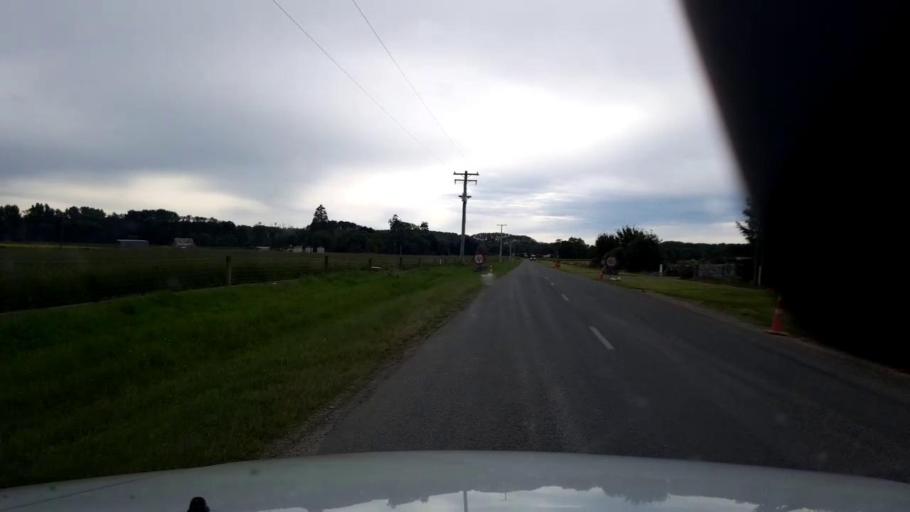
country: NZ
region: Canterbury
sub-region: Timaru District
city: Pleasant Point
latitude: -44.2702
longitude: 171.2584
